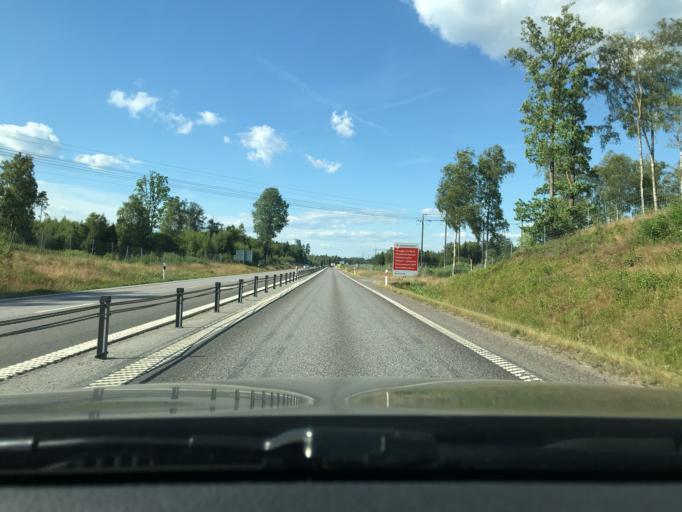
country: SE
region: Kronoberg
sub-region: Almhults Kommun
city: AElmhult
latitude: 56.5245
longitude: 14.1408
